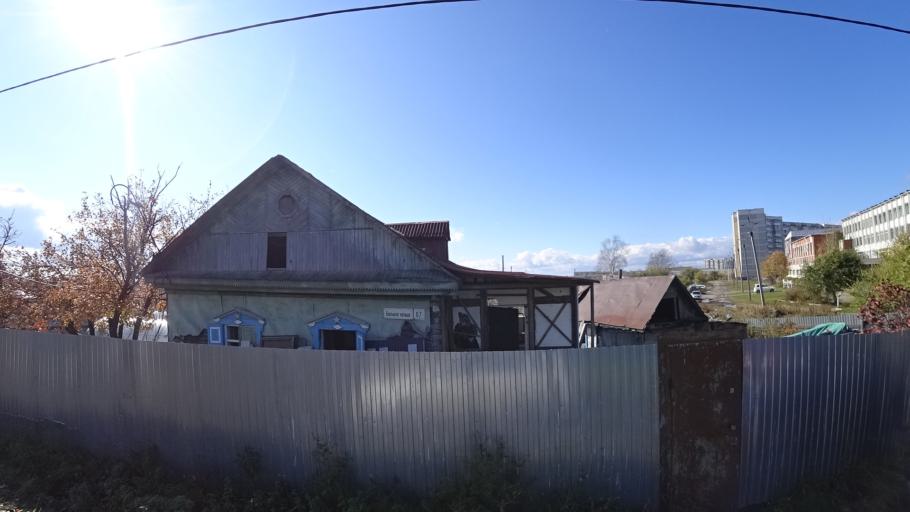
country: RU
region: Khabarovsk Krai
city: Amursk
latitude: 50.2379
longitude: 136.9177
